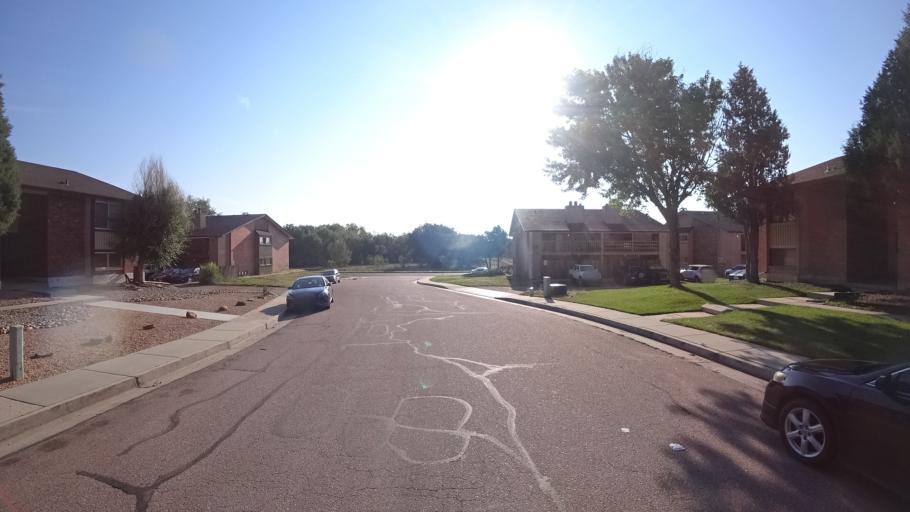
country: US
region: Colorado
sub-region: El Paso County
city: Colorado Springs
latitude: 38.8898
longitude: -104.8452
